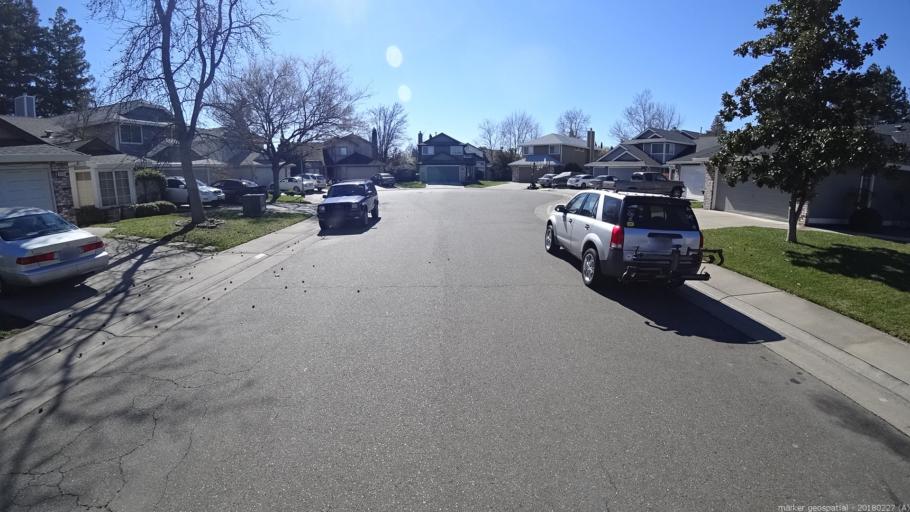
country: US
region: California
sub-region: Sacramento County
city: Antelope
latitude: 38.7170
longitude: -121.3490
